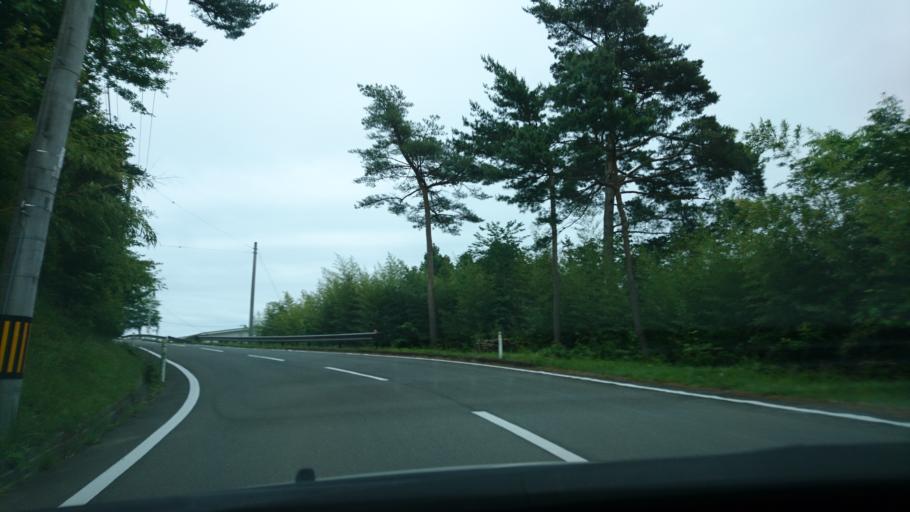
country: JP
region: Miyagi
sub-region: Oshika Gun
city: Onagawa Cho
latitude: 38.7769
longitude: 141.5153
